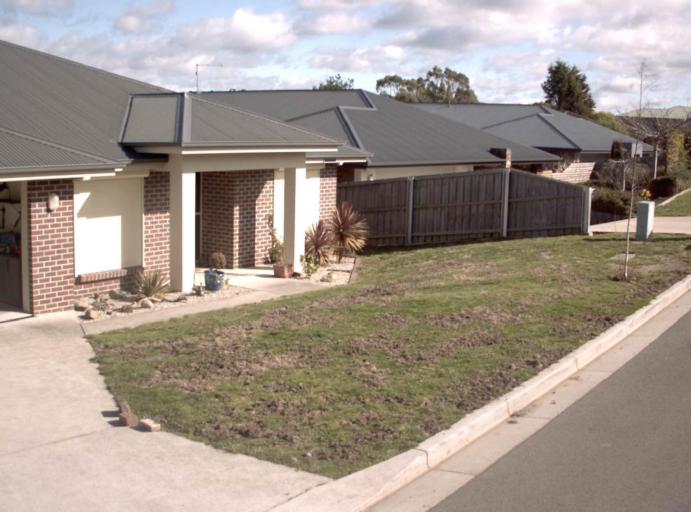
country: AU
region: Tasmania
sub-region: Launceston
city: Summerhill
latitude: -41.4634
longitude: 147.1291
